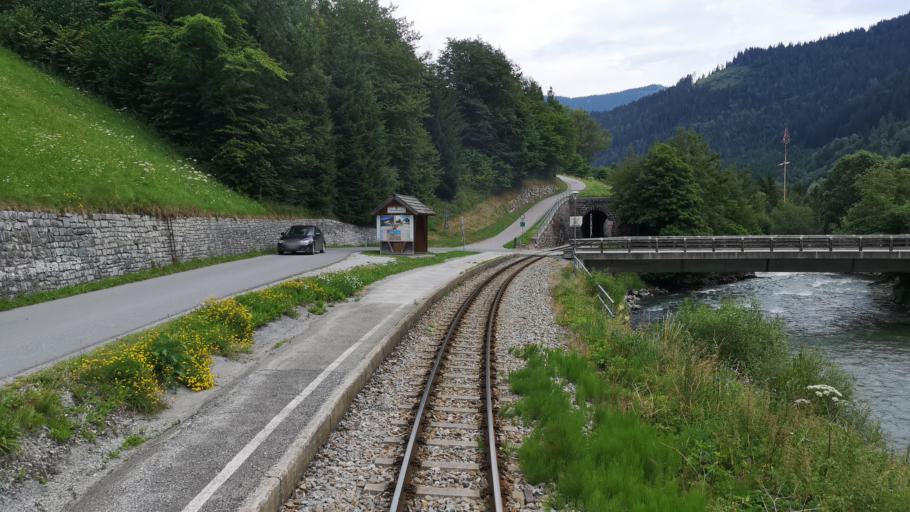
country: AT
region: Salzburg
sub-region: Politischer Bezirk Tamsweg
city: Ramingstein
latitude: 47.0693
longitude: 13.8843
